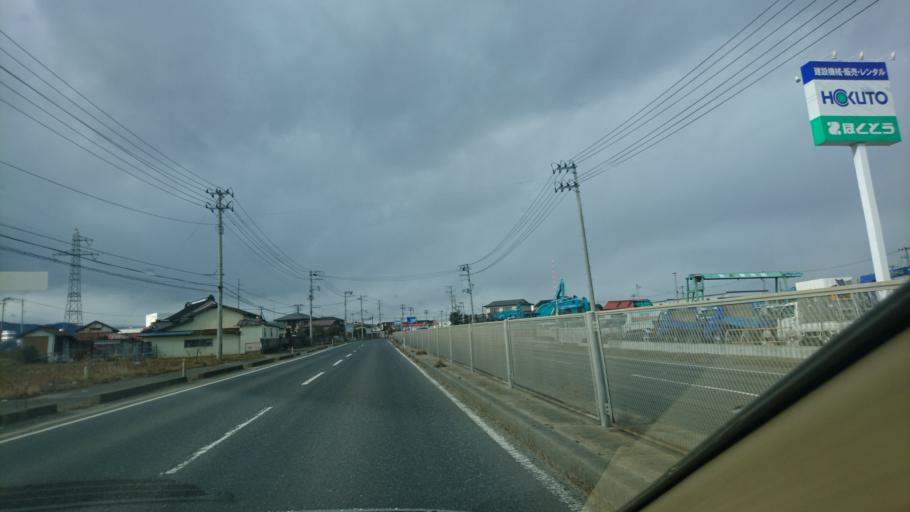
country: JP
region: Miyagi
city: Tomiya
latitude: 38.4377
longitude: 140.9079
